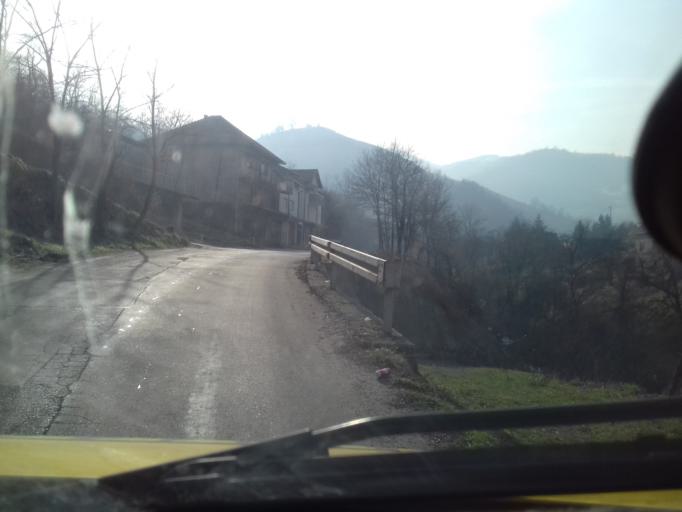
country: BA
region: Federation of Bosnia and Herzegovina
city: Zenica
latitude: 44.1864
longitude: 17.9044
